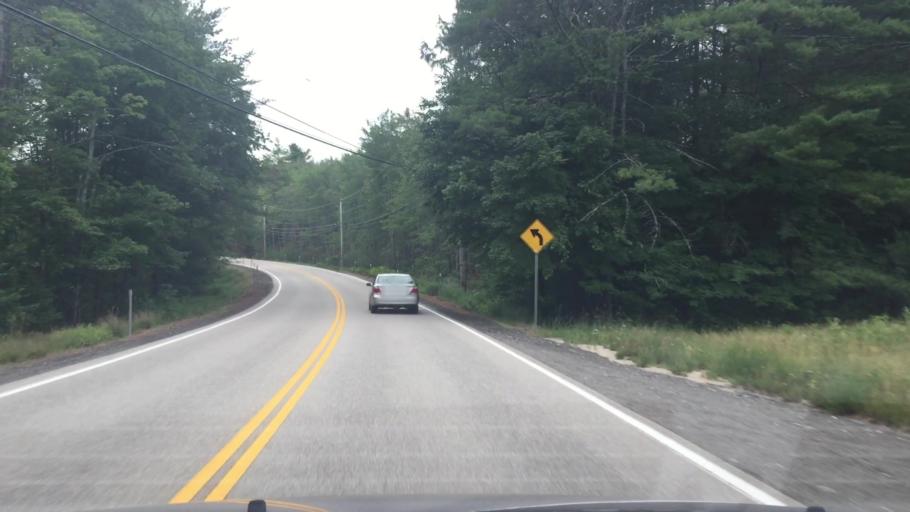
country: US
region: New Hampshire
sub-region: Carroll County
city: Conway
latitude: 43.9660
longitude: -71.1090
